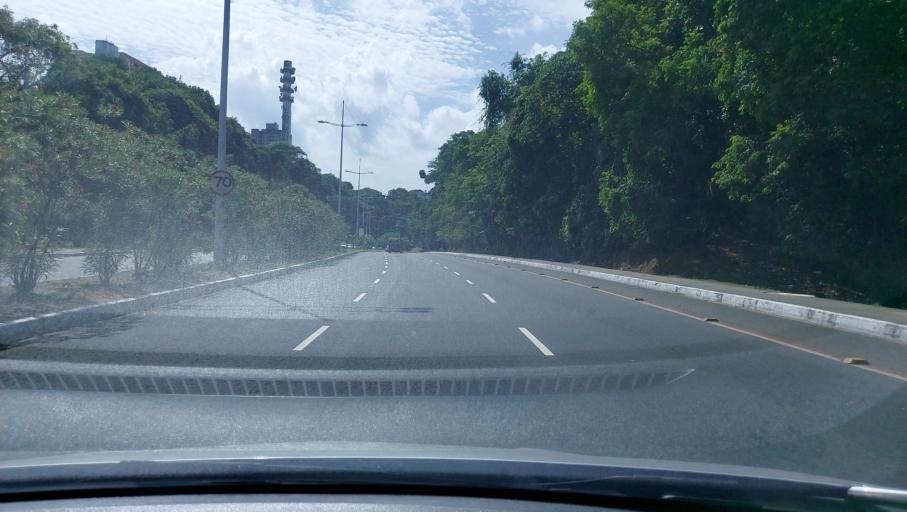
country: BR
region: Bahia
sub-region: Salvador
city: Salvador
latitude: -12.9589
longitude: -38.4628
